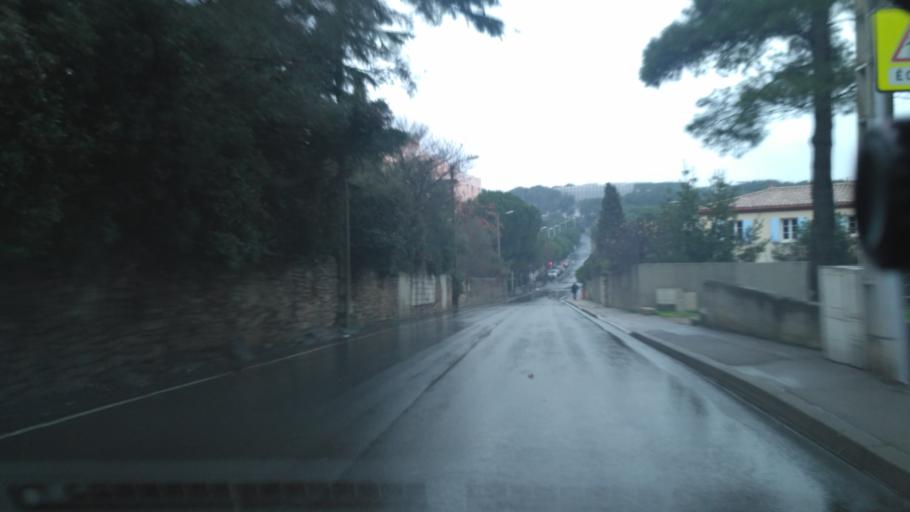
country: FR
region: Languedoc-Roussillon
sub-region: Departement de l'Herault
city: Montpellier
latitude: 43.6353
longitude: 3.8734
